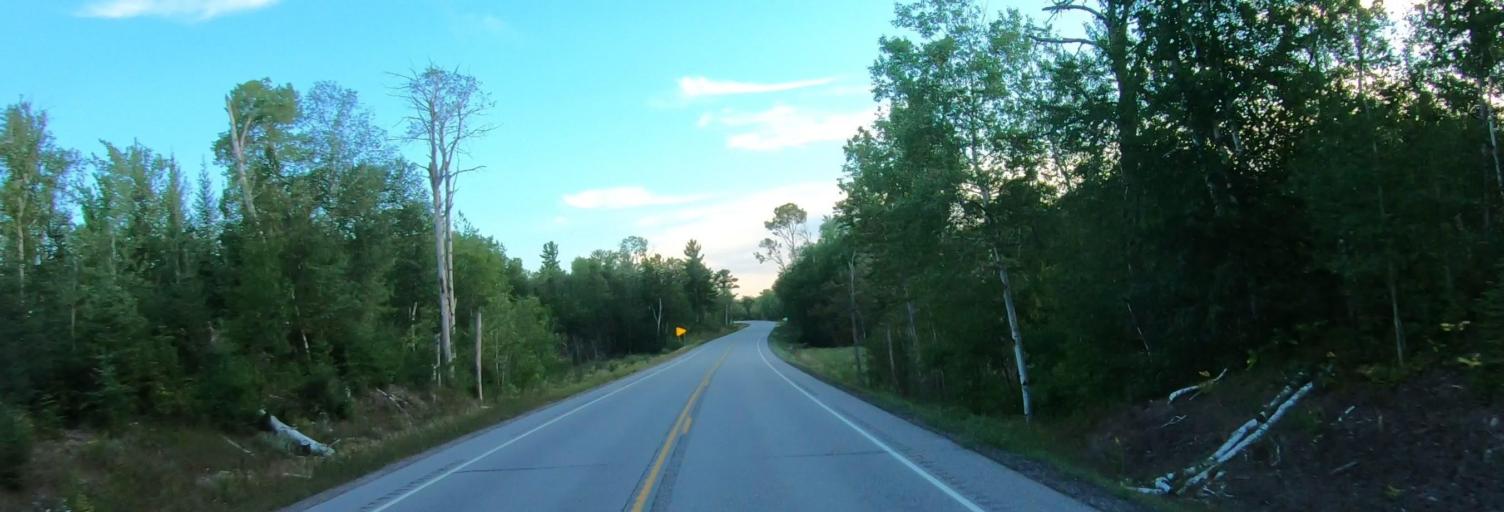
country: US
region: Minnesota
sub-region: Saint Louis County
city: Ely
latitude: 47.8617
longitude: -92.0384
